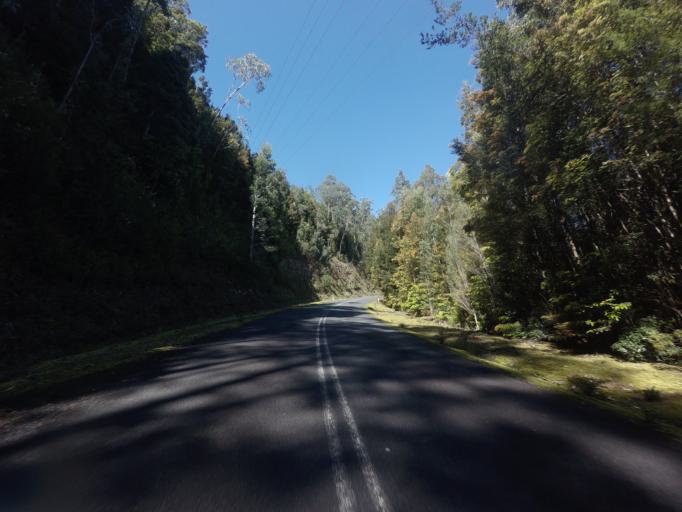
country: AU
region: Tasmania
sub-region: Huon Valley
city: Geeveston
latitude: -42.8194
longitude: 146.3360
